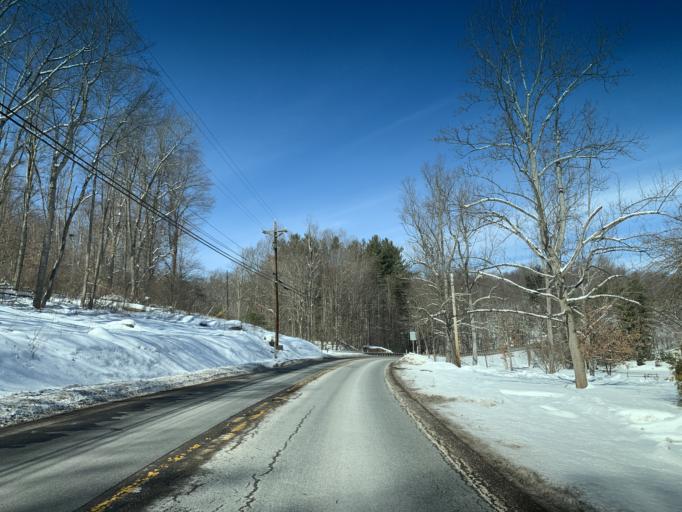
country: US
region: West Virginia
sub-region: Preston County
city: Terra Alta
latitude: 39.6648
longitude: -79.4525
